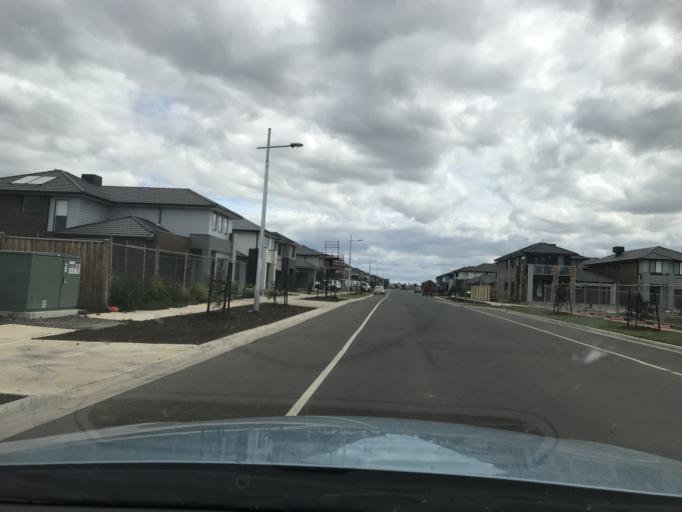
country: AU
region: Victoria
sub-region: Wyndham
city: Williams Landing
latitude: -37.8652
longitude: 144.7562
